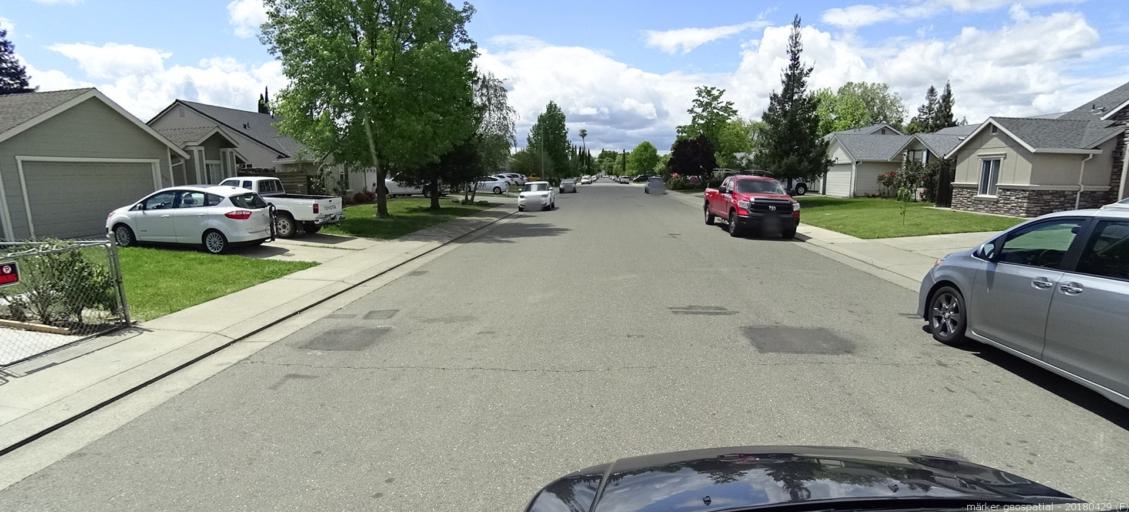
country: US
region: California
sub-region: Yolo County
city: West Sacramento
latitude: 38.5960
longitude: -121.5342
